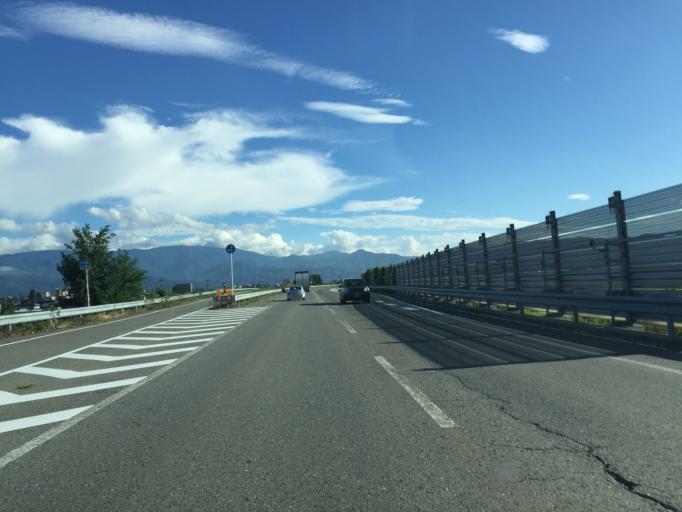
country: JP
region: Yamagata
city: Yonezawa
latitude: 37.9380
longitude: 140.1112
